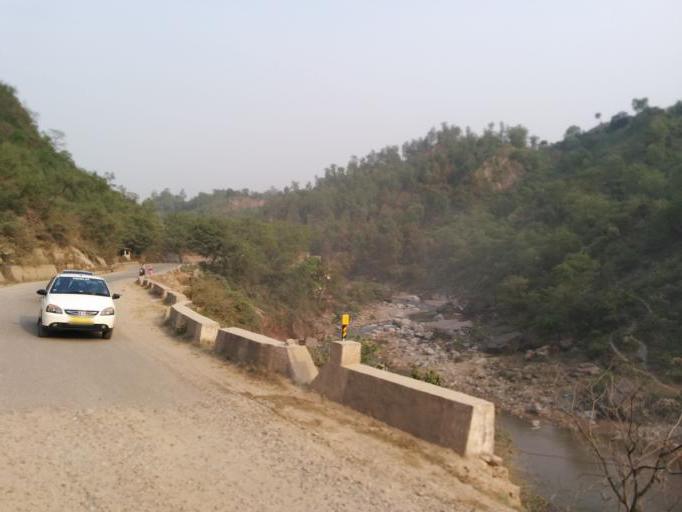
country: IN
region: Himachal Pradesh
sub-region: Kangra
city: Kotla
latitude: 32.2301
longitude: 76.0705
